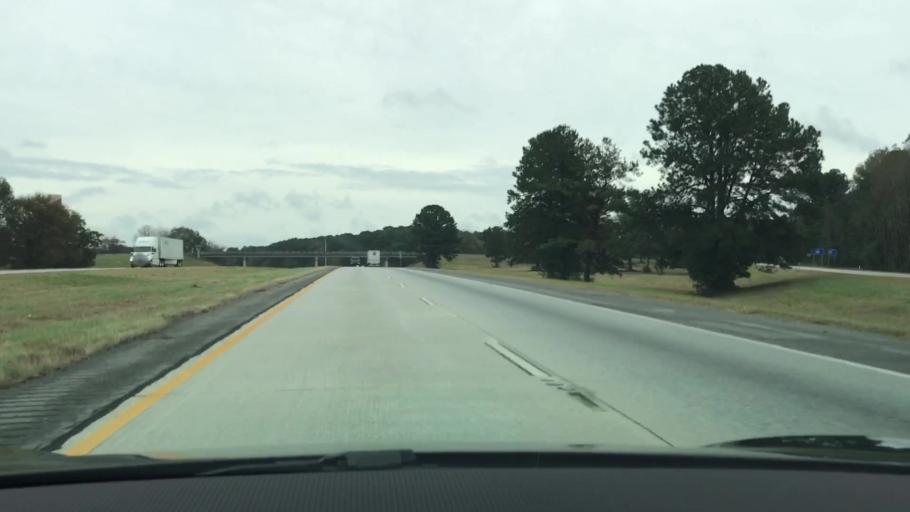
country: US
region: Georgia
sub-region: Greene County
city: Union Point
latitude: 33.5444
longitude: -83.0832
